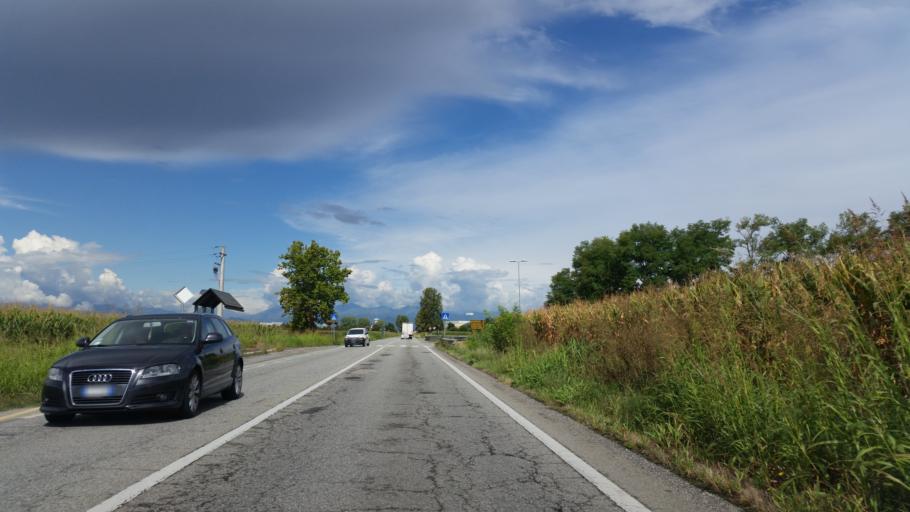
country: IT
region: Piedmont
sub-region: Provincia di Torino
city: Marocchi
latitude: 44.9476
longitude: 7.8059
